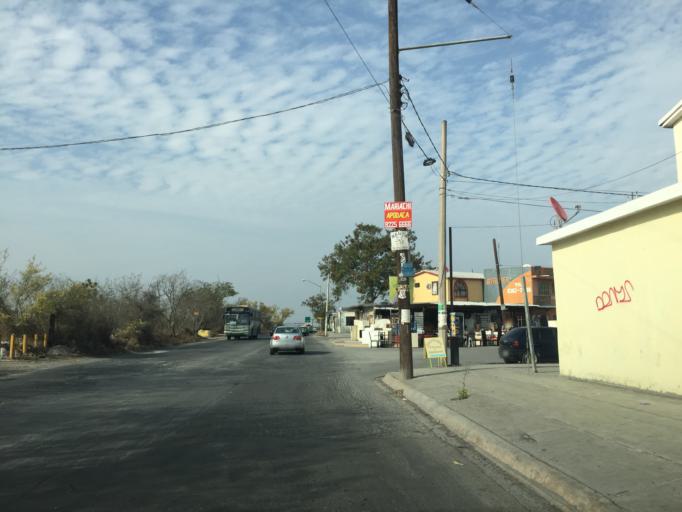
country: MX
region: Nuevo Leon
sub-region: Apodaca
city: Fraccionamiento Cosmopolis Octavo Sector
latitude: 25.7978
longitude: -100.2485
